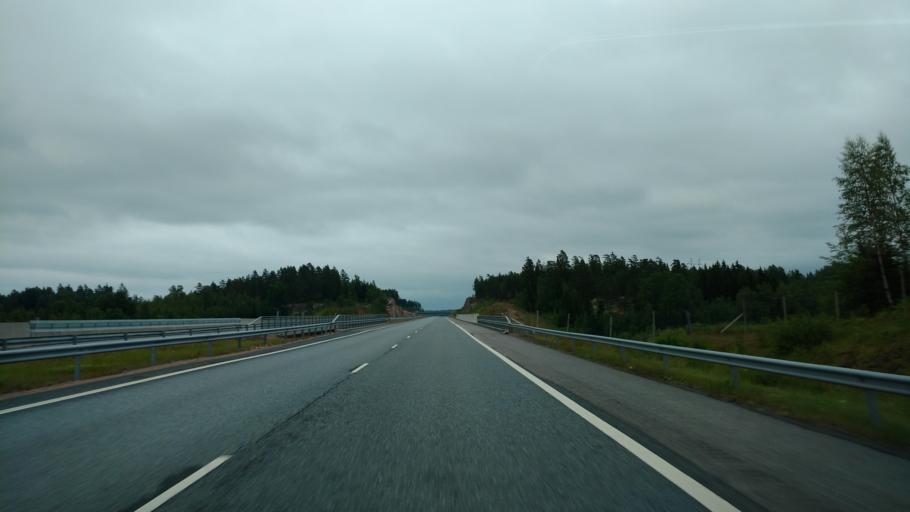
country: FI
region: Varsinais-Suomi
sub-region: Salo
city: Kiikala
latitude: 60.3917
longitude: 23.5379
